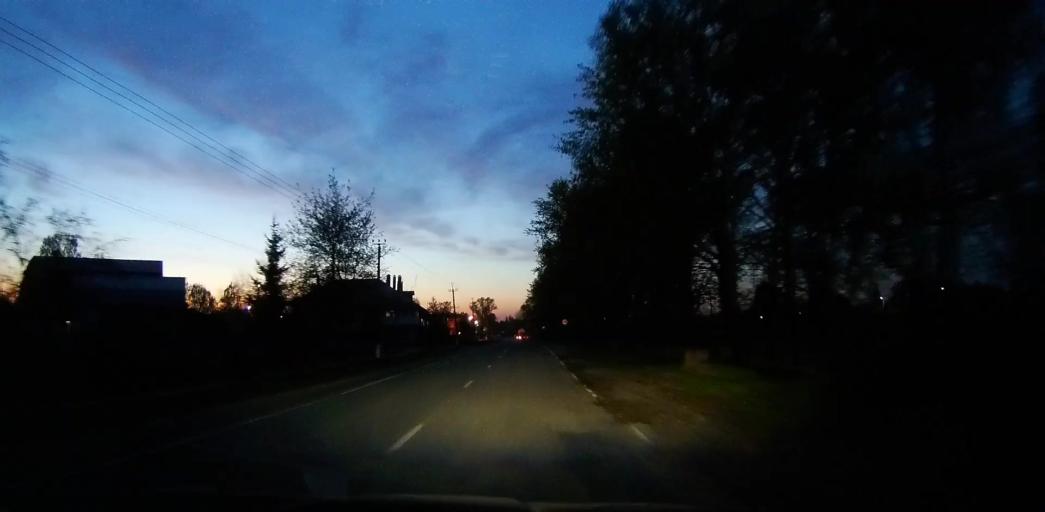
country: RU
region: Moskovskaya
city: Peski
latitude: 55.2127
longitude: 38.7721
